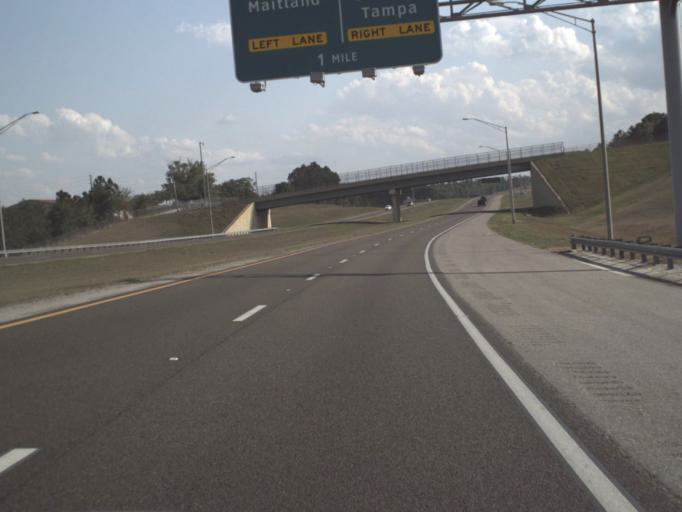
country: US
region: Florida
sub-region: Orange County
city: Apopka
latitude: 28.6726
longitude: -81.5264
